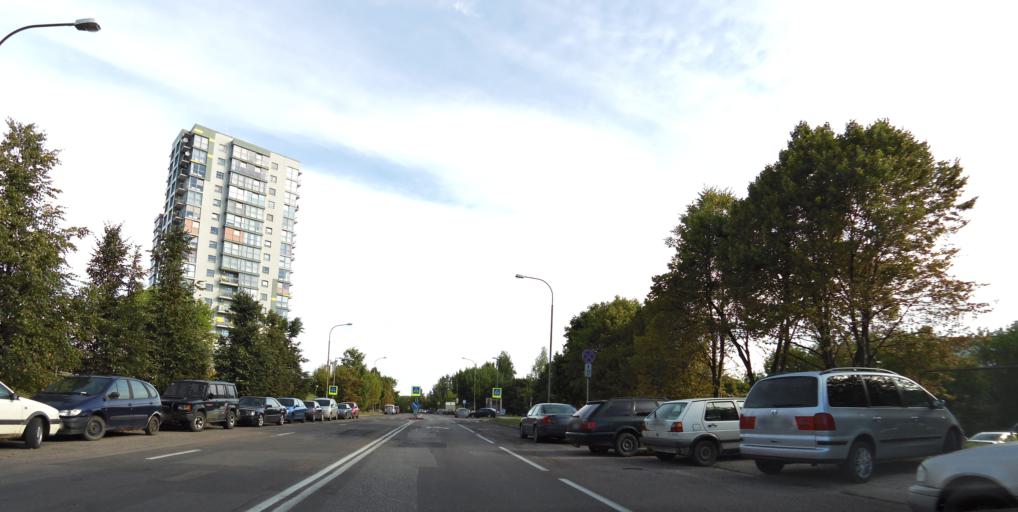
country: LT
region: Vilnius County
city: Seskine
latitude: 54.7122
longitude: 25.2511
